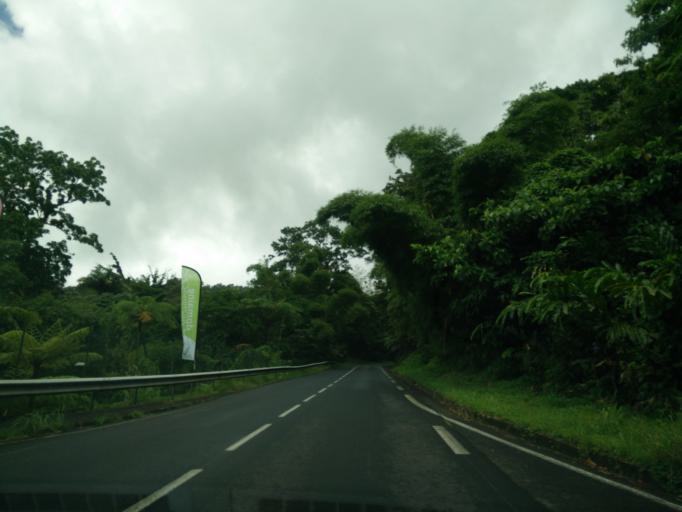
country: MQ
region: Martinique
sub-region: Martinique
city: Le Morne-Rouge
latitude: 14.7491
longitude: -61.1019
